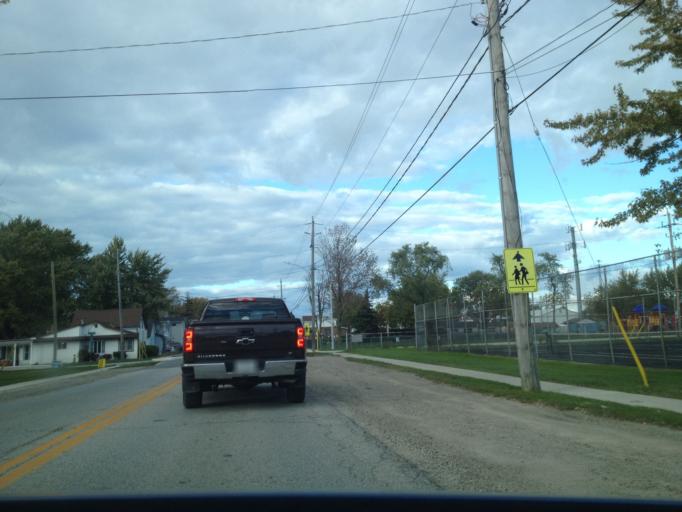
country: US
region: Michigan
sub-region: Wayne County
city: Grosse Pointe Farms
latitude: 42.2899
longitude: -82.7119
